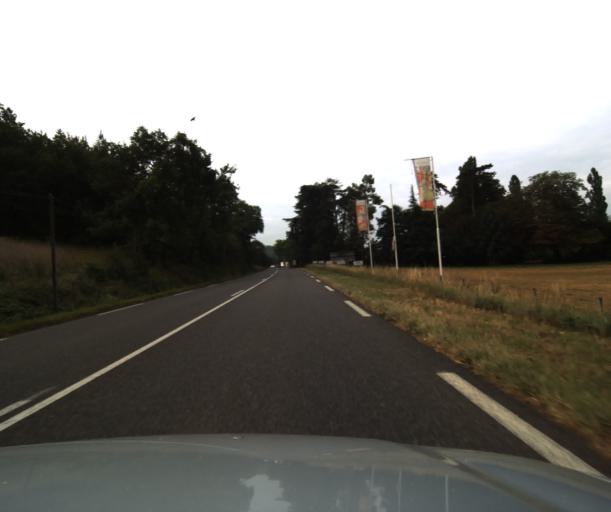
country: FR
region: Midi-Pyrenees
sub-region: Departement du Gers
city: Mirande
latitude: 43.5243
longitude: 0.4170
